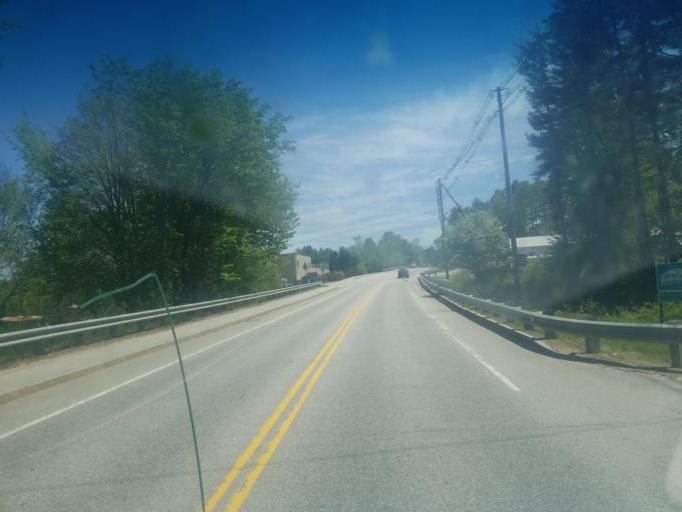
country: US
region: New Hampshire
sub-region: Grafton County
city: Plymouth
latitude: 43.7691
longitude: -71.7188
